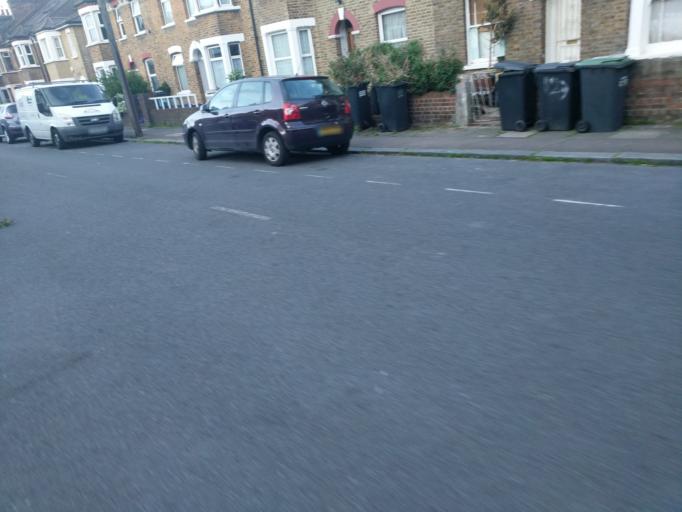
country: GB
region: England
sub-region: Greater London
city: Catford
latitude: 51.4584
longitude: -0.0179
